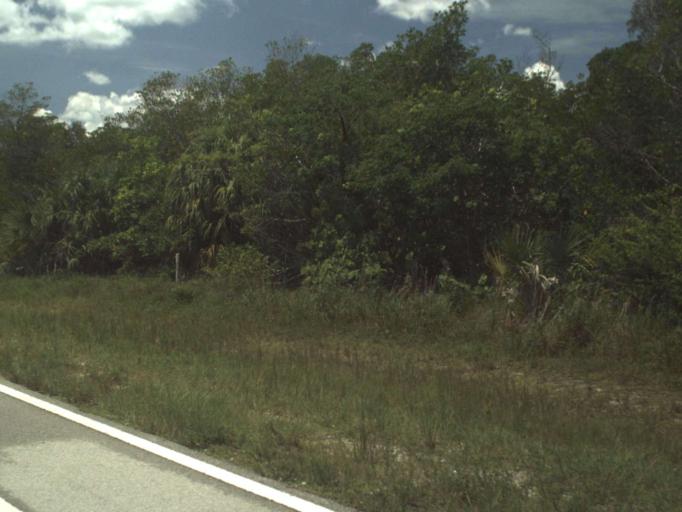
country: US
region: Florida
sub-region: Saint Lucie County
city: Hutchinson Island South
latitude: 27.3366
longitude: -80.2356
